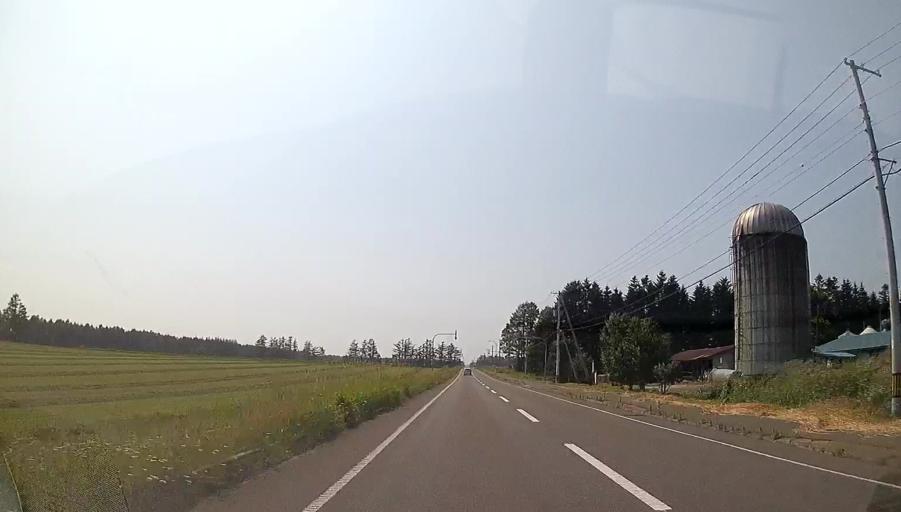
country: JP
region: Hokkaido
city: Otofuke
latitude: 43.1723
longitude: 143.1000
